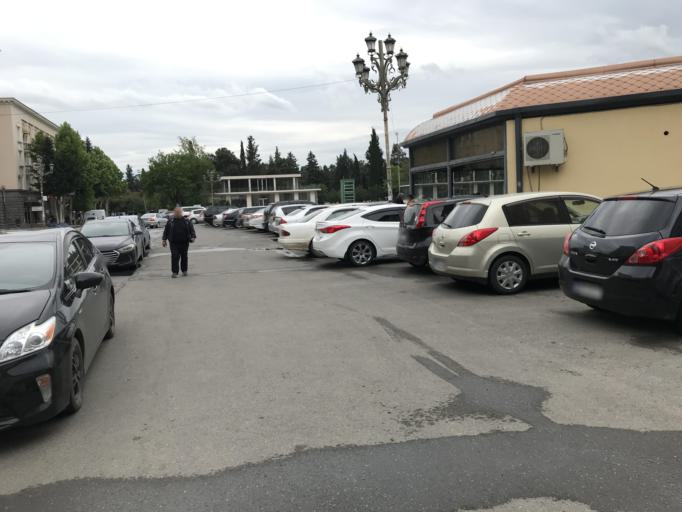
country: GE
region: Kvemo Kartli
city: Rust'avi
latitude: 41.5435
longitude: 45.0122
